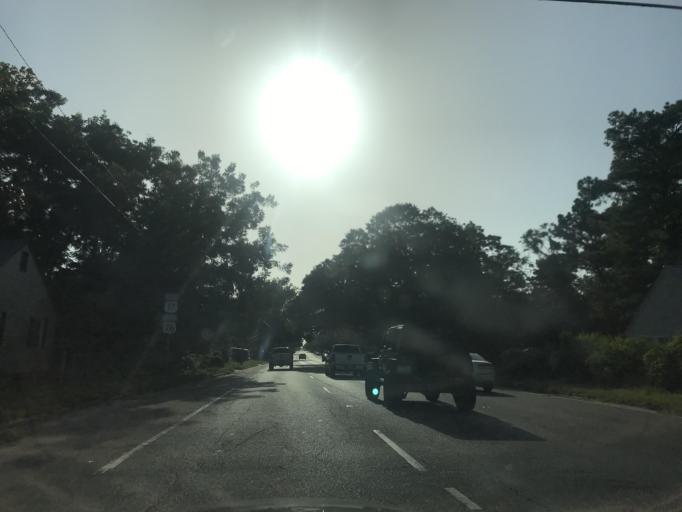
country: US
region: North Carolina
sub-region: New Hanover County
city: Wilmington
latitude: 34.2268
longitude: -77.9277
